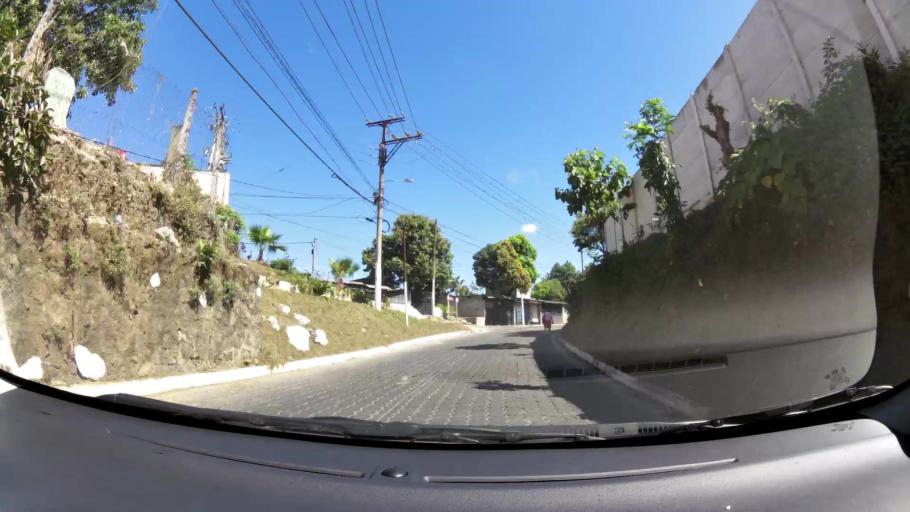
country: SV
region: San Salvador
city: Apopa
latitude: 13.8051
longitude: -89.1854
